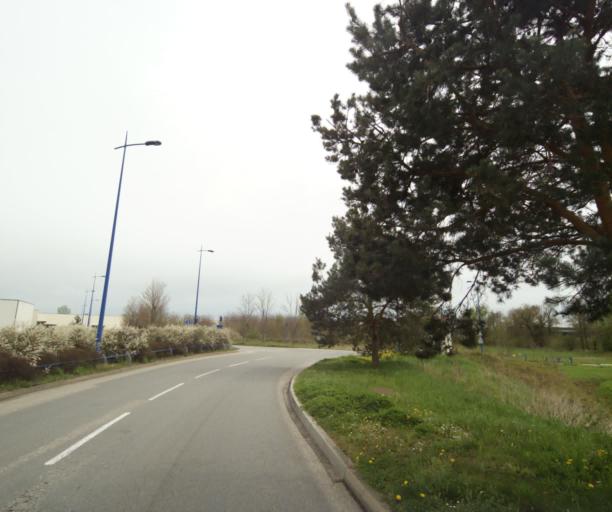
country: FR
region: Bourgogne
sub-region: Departement de Saone-et-Loire
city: Charnay-les-Macon
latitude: 46.2837
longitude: 4.7846
